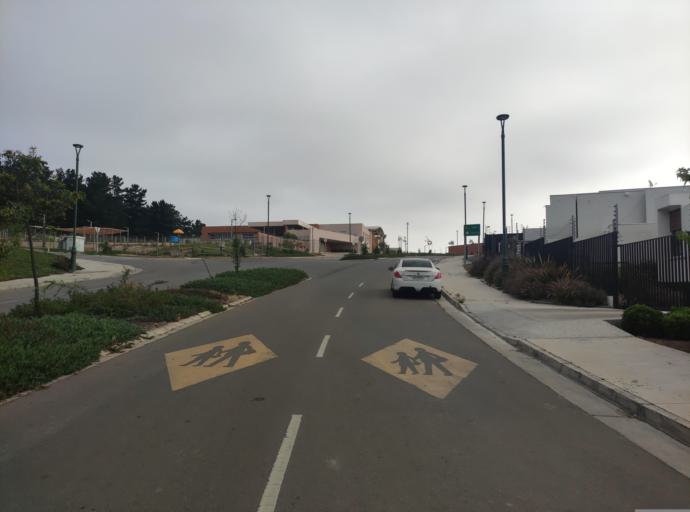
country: CL
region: Valparaiso
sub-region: Provincia de Valparaiso
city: Vina del Mar
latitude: -32.9445
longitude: -71.5321
